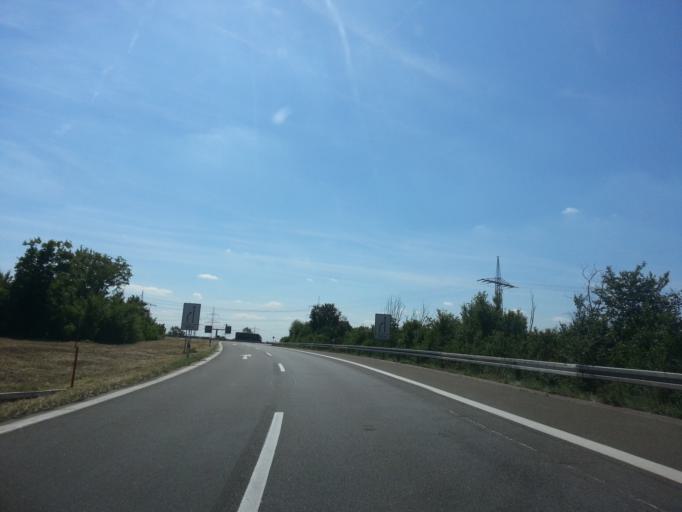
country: DE
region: Baden-Wuerttemberg
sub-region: Karlsruhe Region
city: Ilvesheim
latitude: 49.4603
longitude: 8.5378
